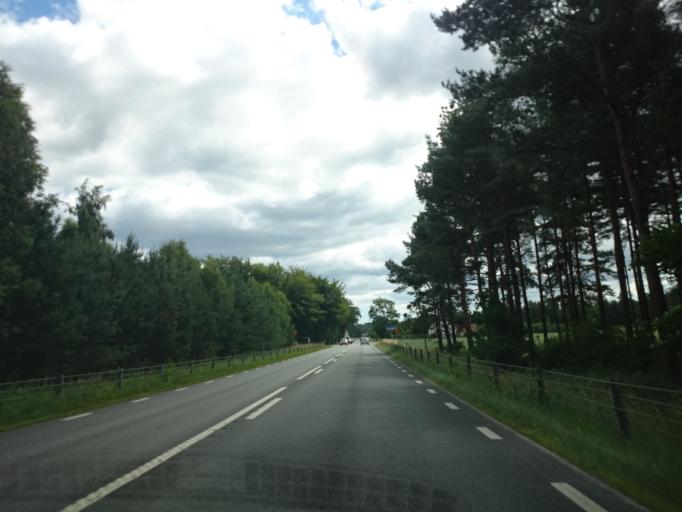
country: SE
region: Skane
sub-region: Kristianstads Kommun
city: Degeberga
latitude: 55.8156
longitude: 14.1316
